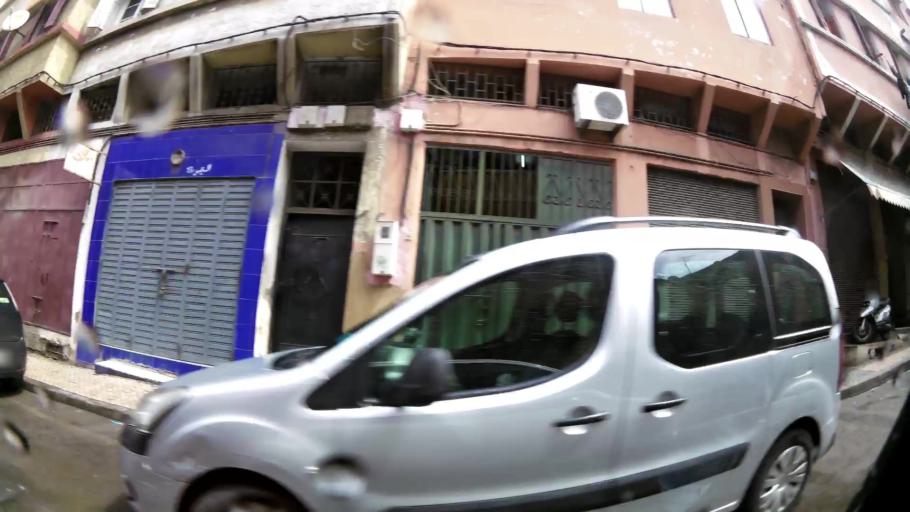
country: MA
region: Grand Casablanca
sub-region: Casablanca
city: Casablanca
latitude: 33.5752
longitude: -7.5945
